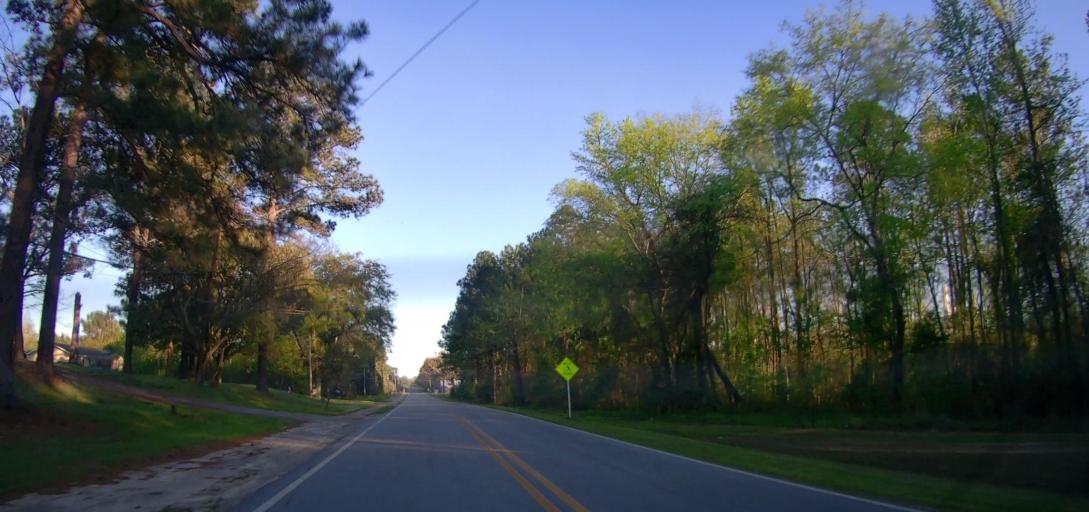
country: US
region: Georgia
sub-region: Wilkinson County
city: Irwinton
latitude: 32.8512
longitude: -83.2173
